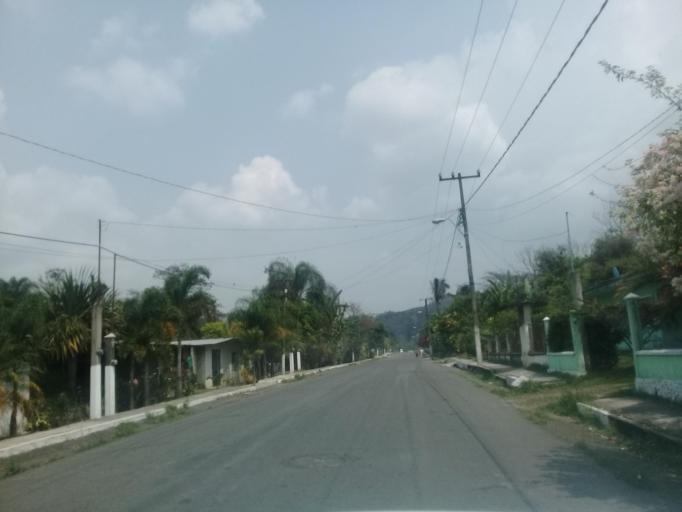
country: MX
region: Veracruz
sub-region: Cordoba
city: San Jose de Tapia
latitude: 18.8204
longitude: -96.9809
